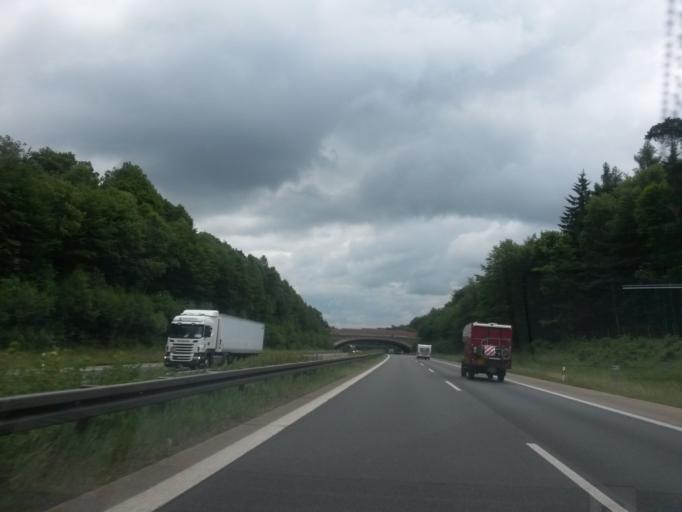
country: DE
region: Bavaria
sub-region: Regierungsbezirk Unterfranken
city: Oberthulba
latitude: 50.2189
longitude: 9.9054
